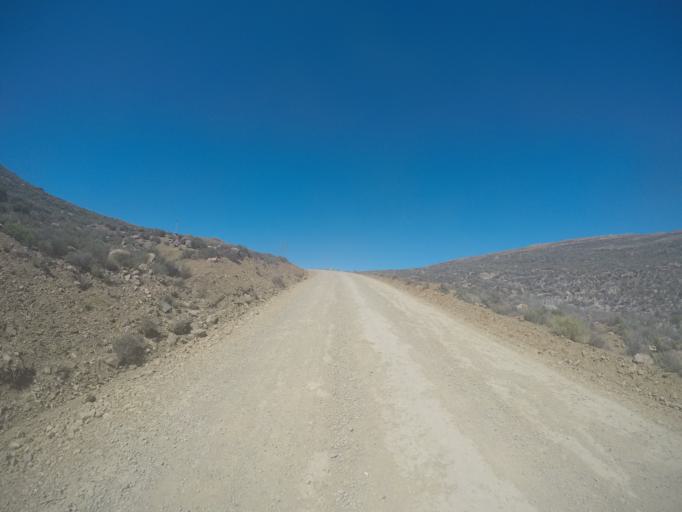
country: ZA
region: Western Cape
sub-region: West Coast District Municipality
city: Clanwilliam
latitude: -32.6089
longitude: 19.3674
